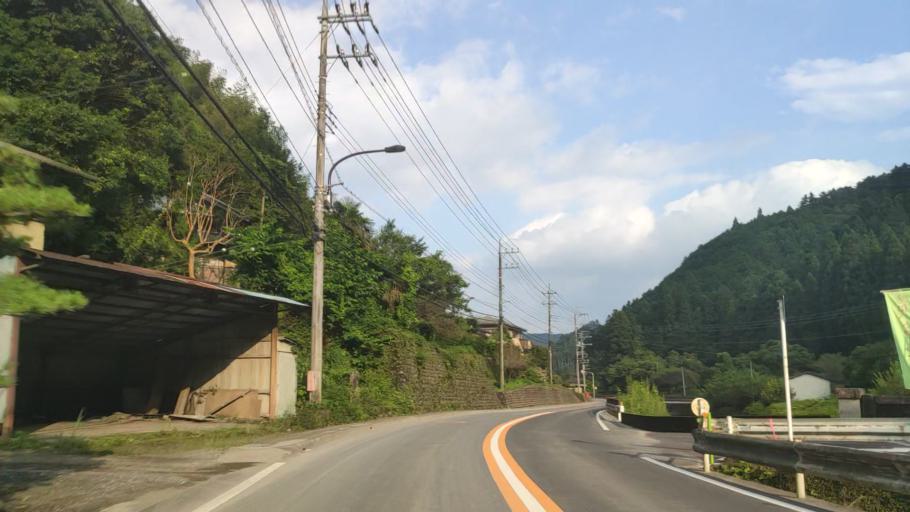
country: JP
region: Tokyo
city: Ome
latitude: 35.8309
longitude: 139.2363
